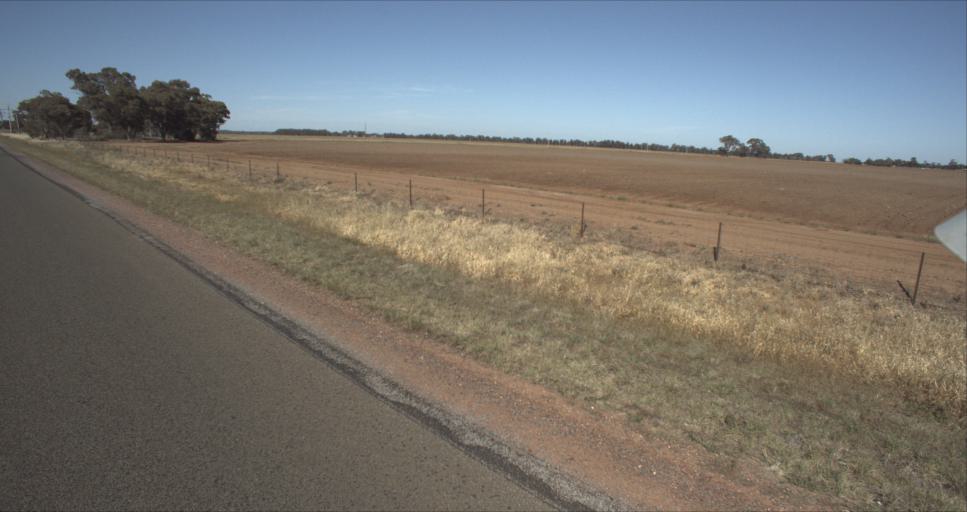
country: AU
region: New South Wales
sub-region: Leeton
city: Leeton
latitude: -34.5752
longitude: 146.2627
